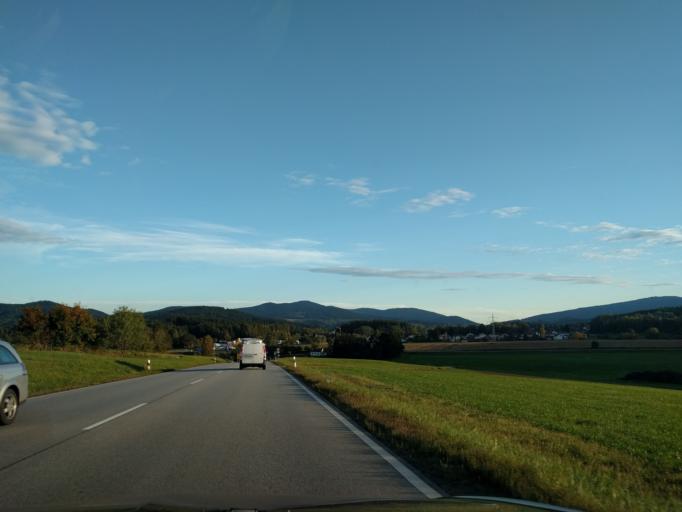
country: DE
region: Bavaria
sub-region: Lower Bavaria
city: Patersdorf
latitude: 49.0181
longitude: 12.9777
